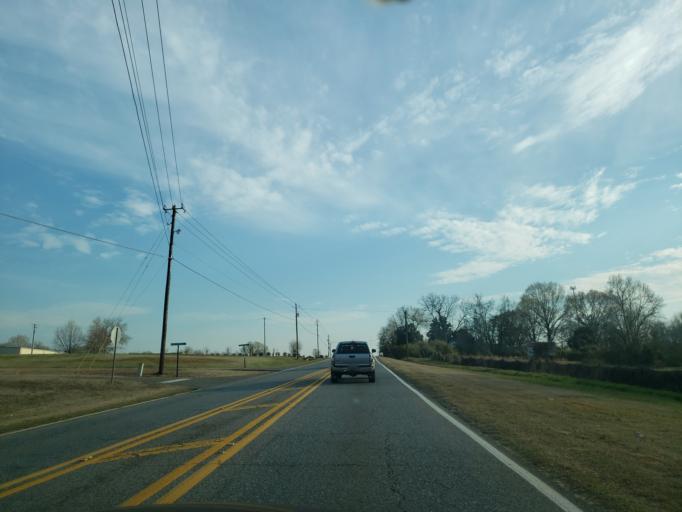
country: US
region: Alabama
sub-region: Hale County
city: Moundville
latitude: 32.9931
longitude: -87.6243
